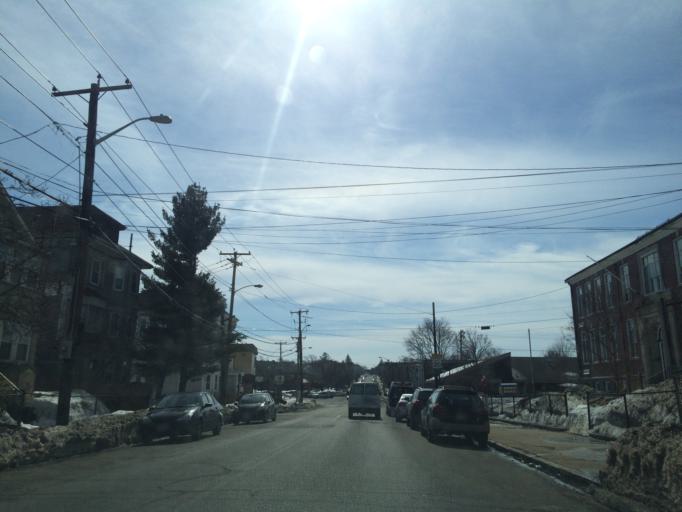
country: US
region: Massachusetts
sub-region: Middlesex County
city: Medford
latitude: 42.4034
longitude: -71.1071
